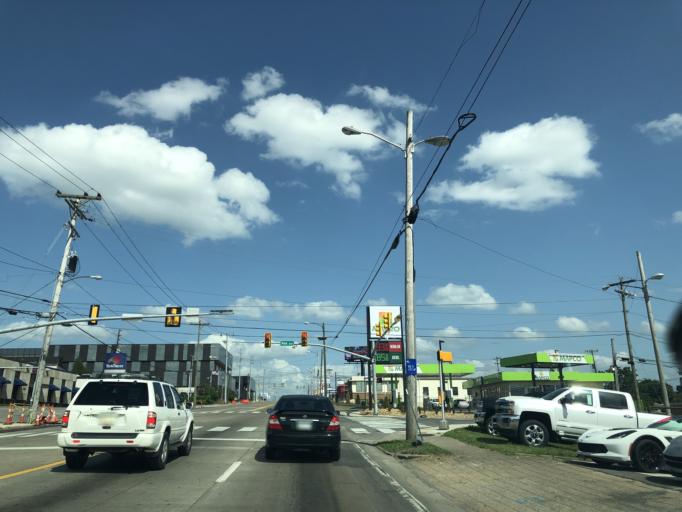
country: US
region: Tennessee
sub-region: Davidson County
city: Nashville
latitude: 36.1424
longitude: -86.7433
